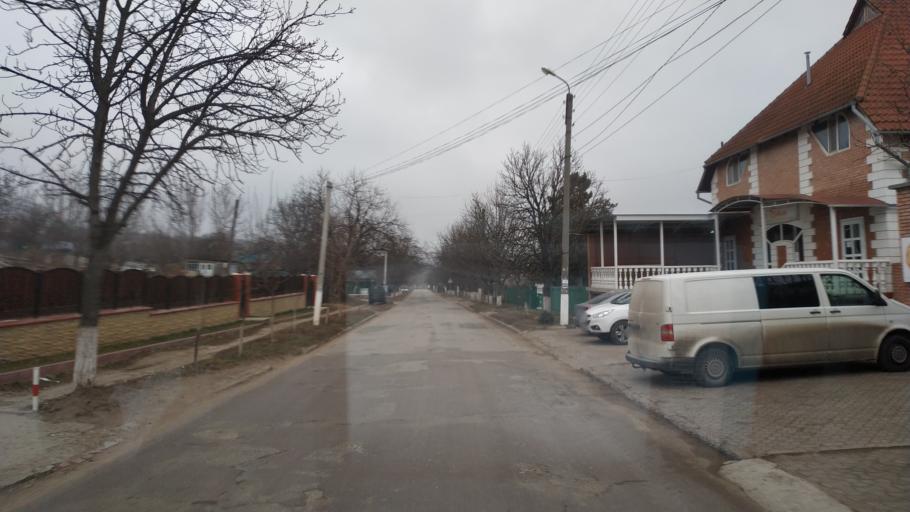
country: MD
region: Hincesti
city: Hincesti
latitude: 46.9041
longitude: 28.6739
